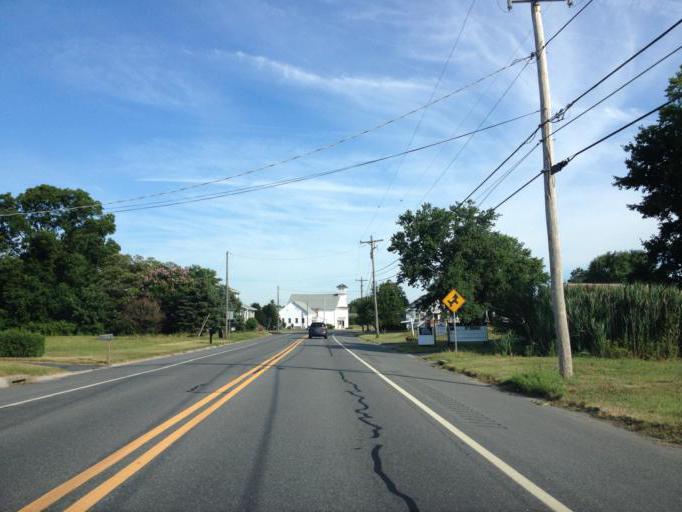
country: US
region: Delaware
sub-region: Sussex County
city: Selbyville
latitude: 38.4921
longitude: -75.1659
